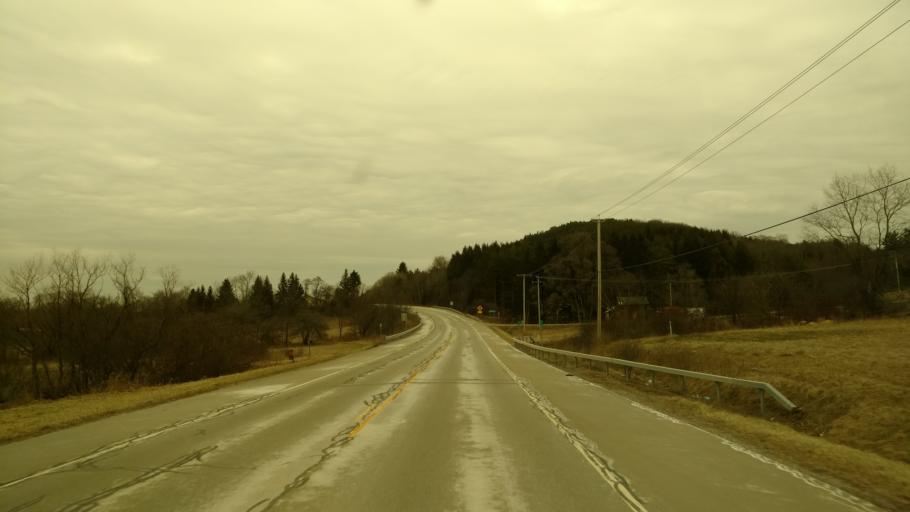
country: US
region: New York
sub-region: Allegany County
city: Wellsville
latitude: 42.0547
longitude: -77.9158
